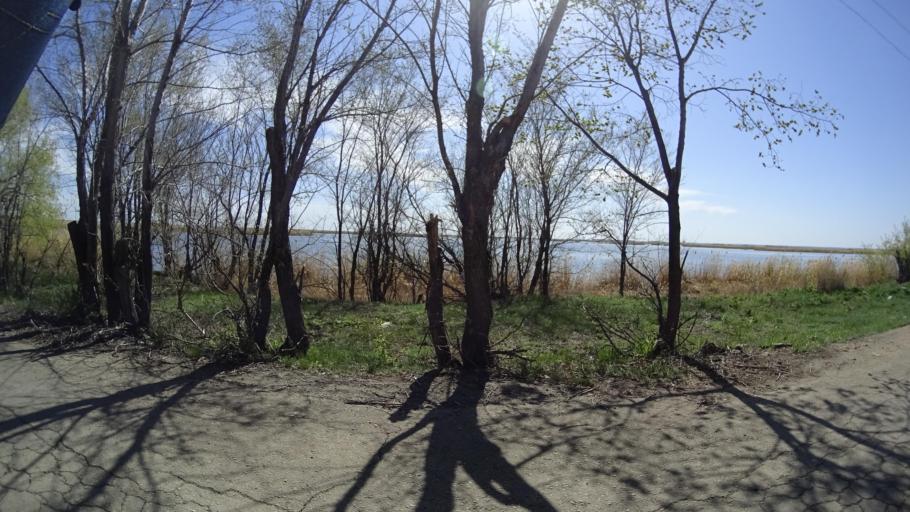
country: RU
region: Chelyabinsk
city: Chesma
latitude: 53.7961
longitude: 61.0271
